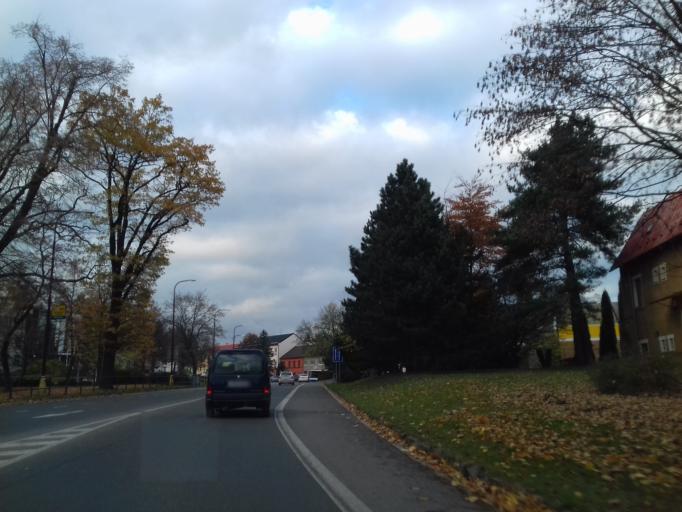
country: CZ
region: Pardubicky
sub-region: Okres Svitavy
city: Svitavy
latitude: 49.7555
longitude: 16.4659
